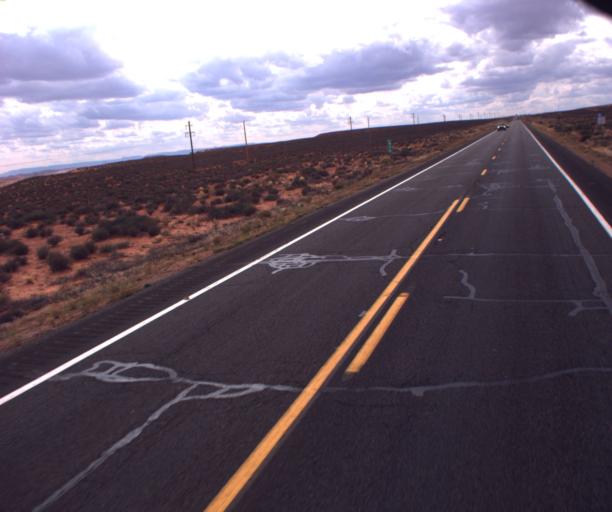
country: US
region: Arizona
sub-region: Navajo County
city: Kayenta
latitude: 36.9255
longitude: -109.7567
